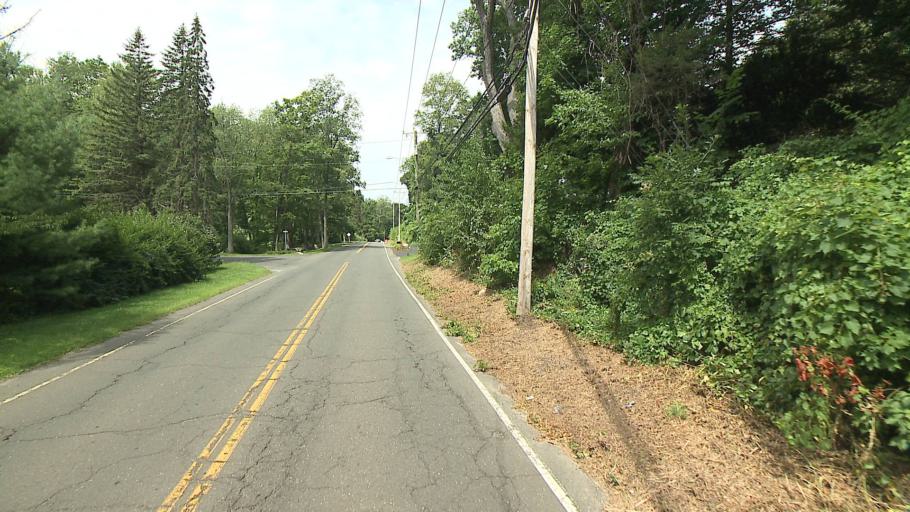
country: US
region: New York
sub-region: Putnam County
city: Putnam Lake
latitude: 41.4669
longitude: -73.4964
